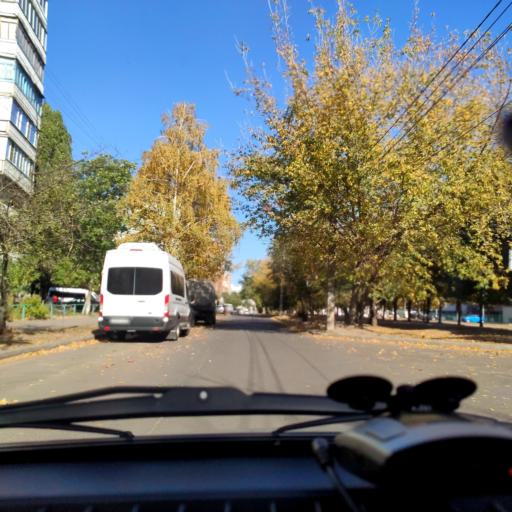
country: RU
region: Voronezj
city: Podgornoye
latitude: 51.7097
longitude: 39.1579
